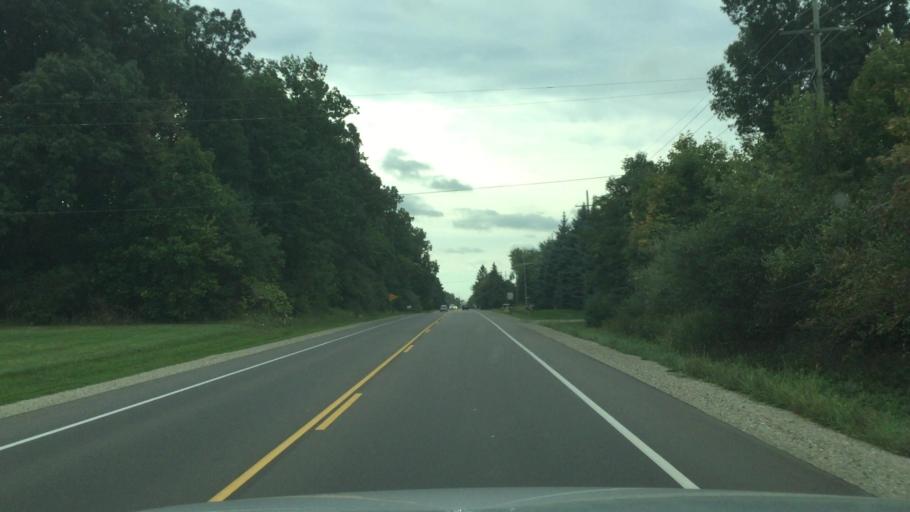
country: US
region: Michigan
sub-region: Livingston County
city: Howell
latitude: 42.6084
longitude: -83.8748
